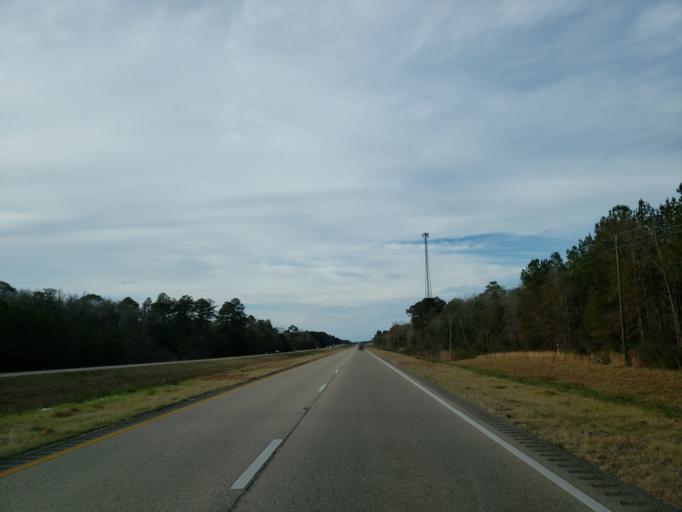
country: US
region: Mississippi
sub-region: Wayne County
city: Belmont
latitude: 31.6116
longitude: -88.5697
